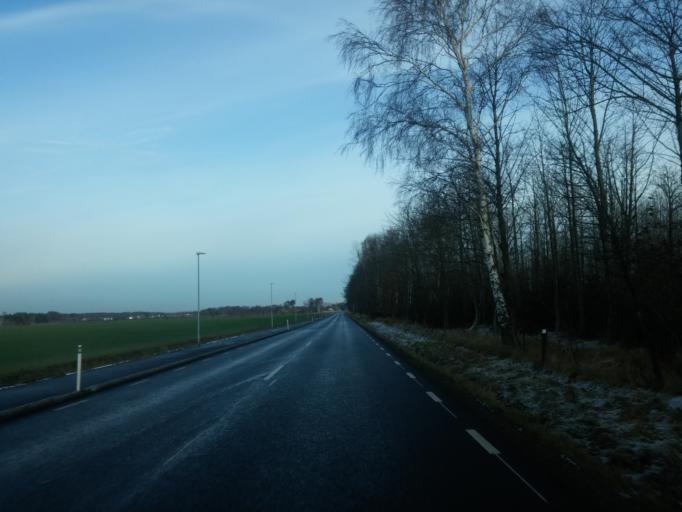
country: SE
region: Skane
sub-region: Angelholms Kommun
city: AEngelholm
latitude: 56.2183
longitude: 12.8151
